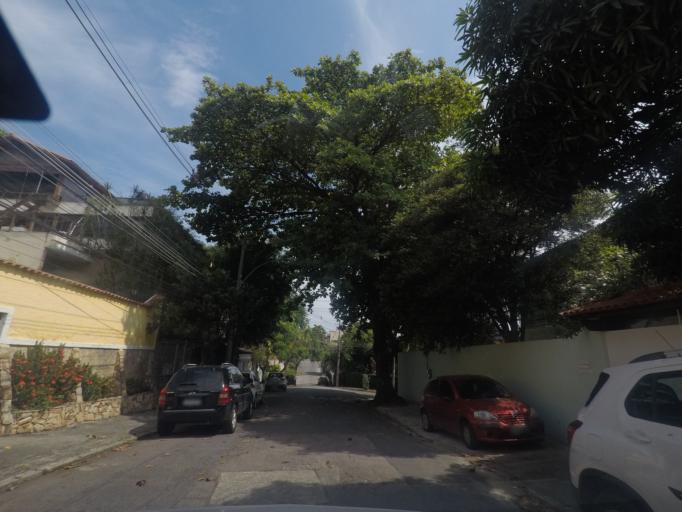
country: BR
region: Rio de Janeiro
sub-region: Rio De Janeiro
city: Rio de Janeiro
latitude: -22.8155
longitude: -43.1998
